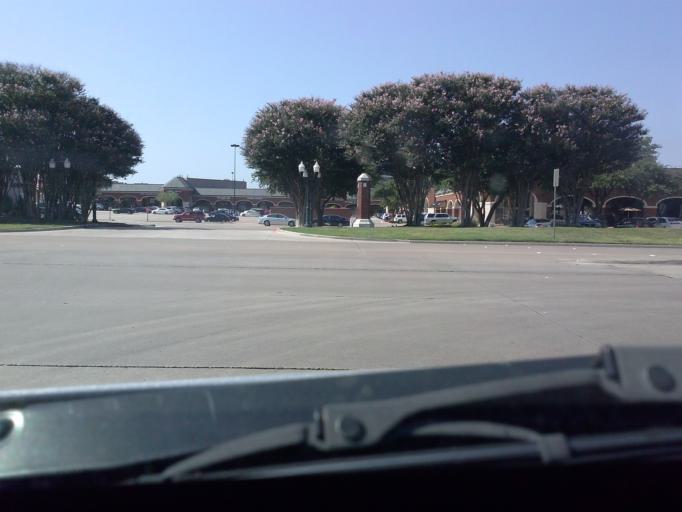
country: US
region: Texas
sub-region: Dallas County
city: Addison
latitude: 33.0272
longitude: -96.7932
